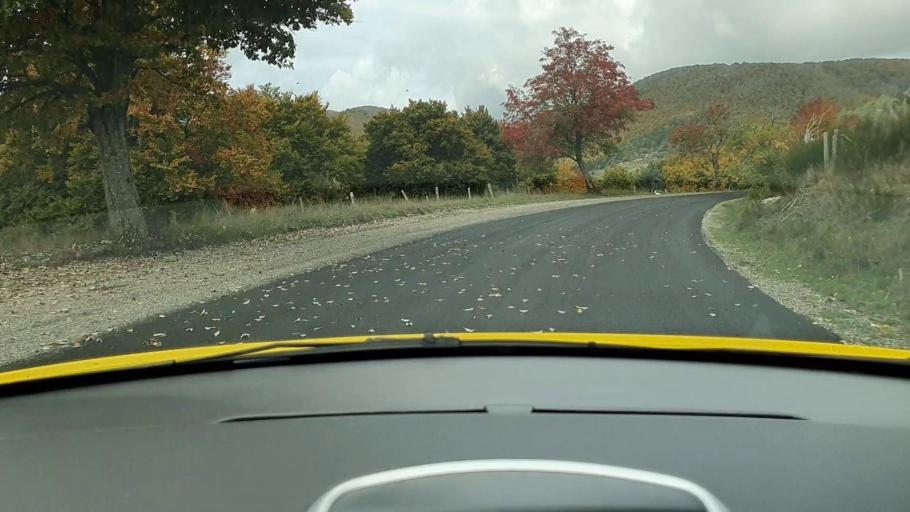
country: FR
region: Languedoc-Roussillon
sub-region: Departement du Gard
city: Valleraugue
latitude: 44.0736
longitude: 3.5341
